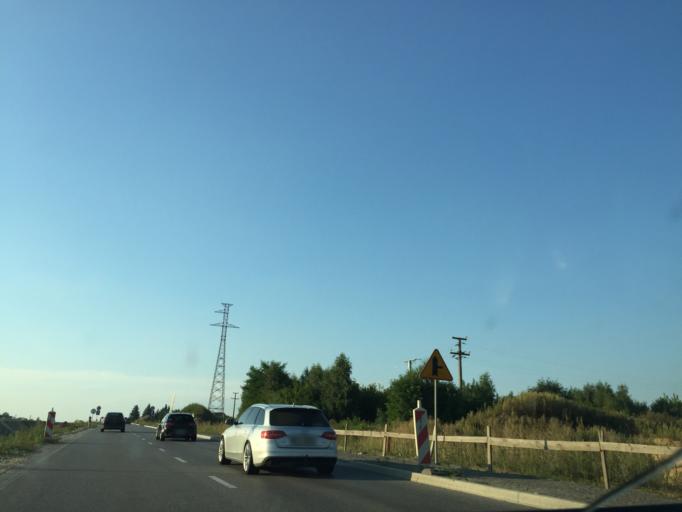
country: PL
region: Masovian Voivodeship
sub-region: Powiat piaseczynski
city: Tarczyn
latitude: 51.9257
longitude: 20.8517
